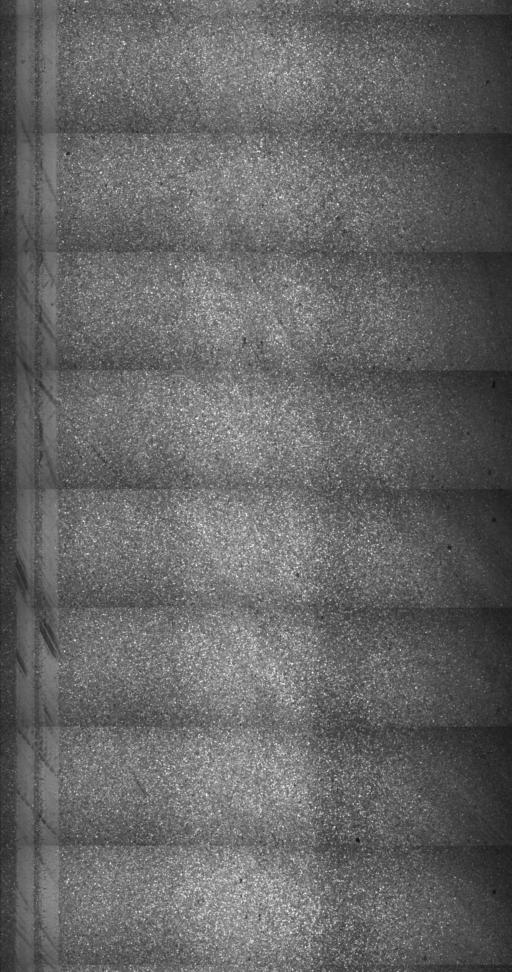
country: US
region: Vermont
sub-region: Addison County
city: Vergennes
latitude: 44.0964
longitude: -73.3002
